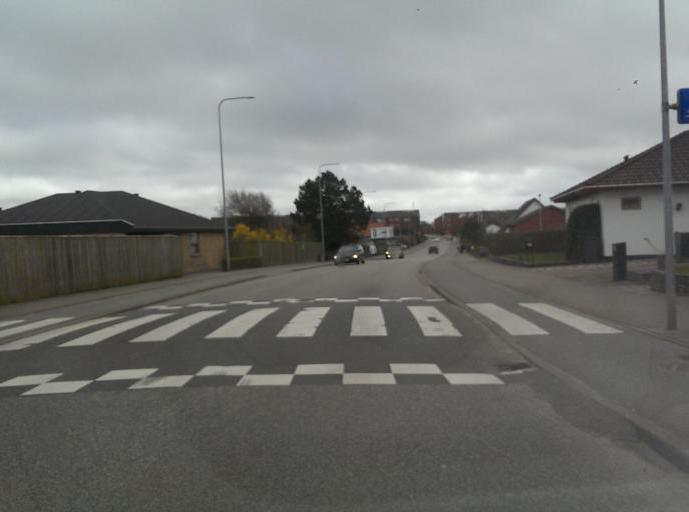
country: DK
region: South Denmark
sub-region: Esbjerg Kommune
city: Esbjerg
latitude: 55.4834
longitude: 8.4786
